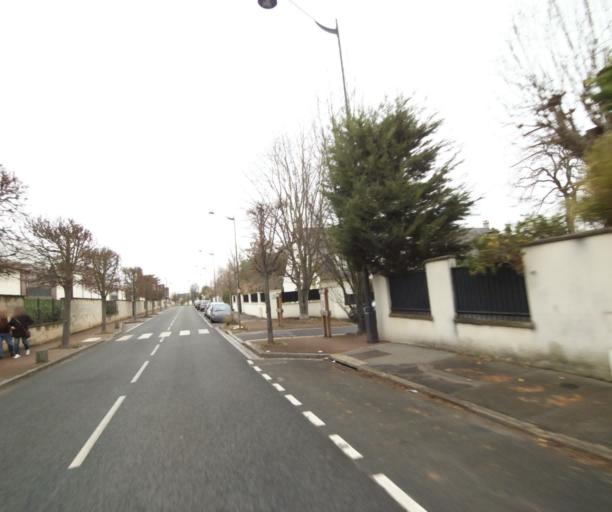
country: FR
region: Ile-de-France
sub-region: Departement des Hauts-de-Seine
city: Garches
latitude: 48.8616
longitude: 2.1732
